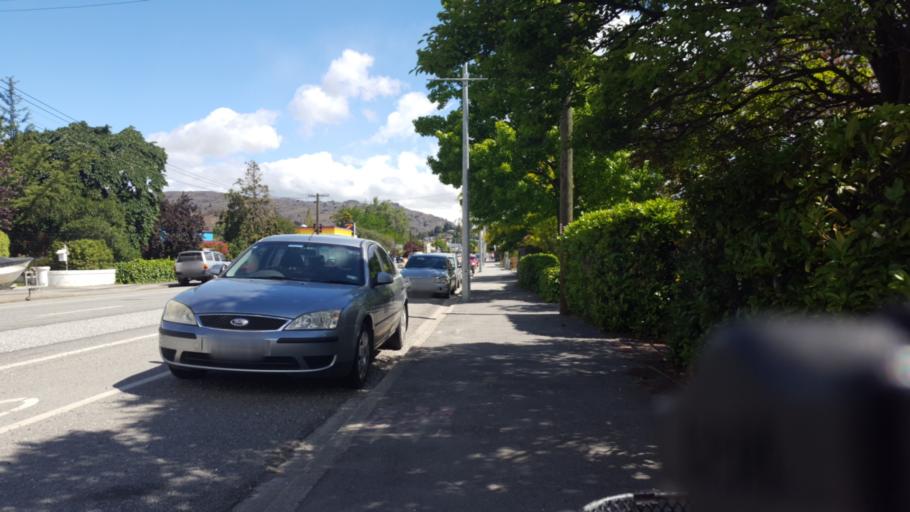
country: NZ
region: Otago
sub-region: Queenstown-Lakes District
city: Wanaka
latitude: -45.2513
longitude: 169.3956
